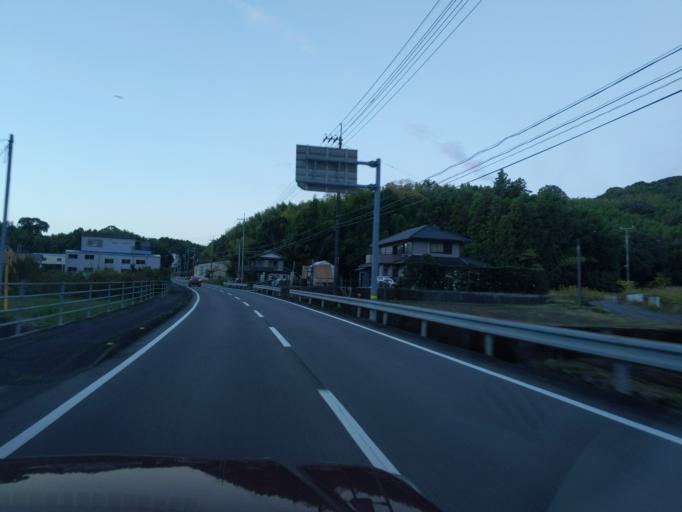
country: JP
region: Tokushima
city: Anan
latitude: 33.8396
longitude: 134.6212
